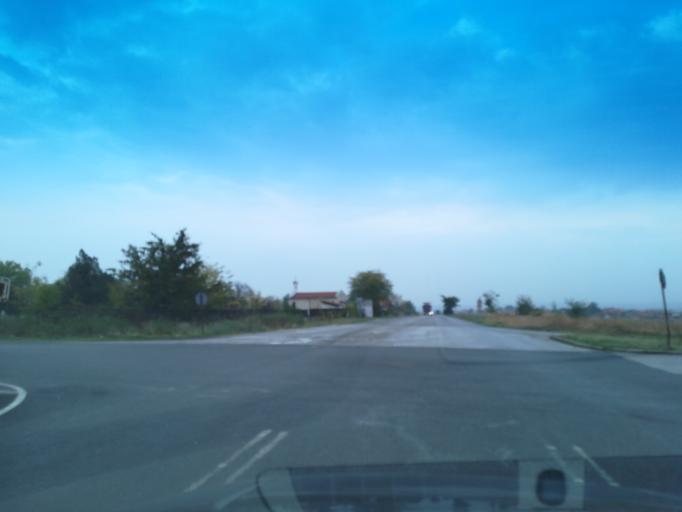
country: BG
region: Stara Zagora
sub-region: Obshtina Chirpan
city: Chirpan
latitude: 42.1961
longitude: 25.3122
